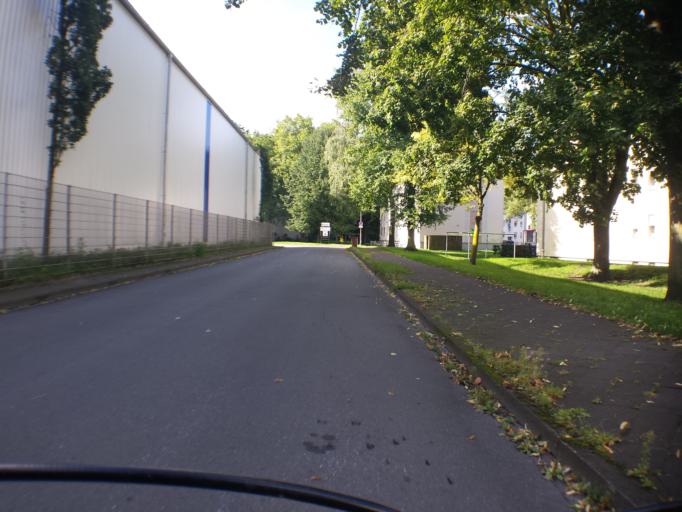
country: DE
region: North Rhine-Westphalia
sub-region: Regierungsbezirk Arnsberg
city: Lippstadt
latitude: 51.6789
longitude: 8.3148
